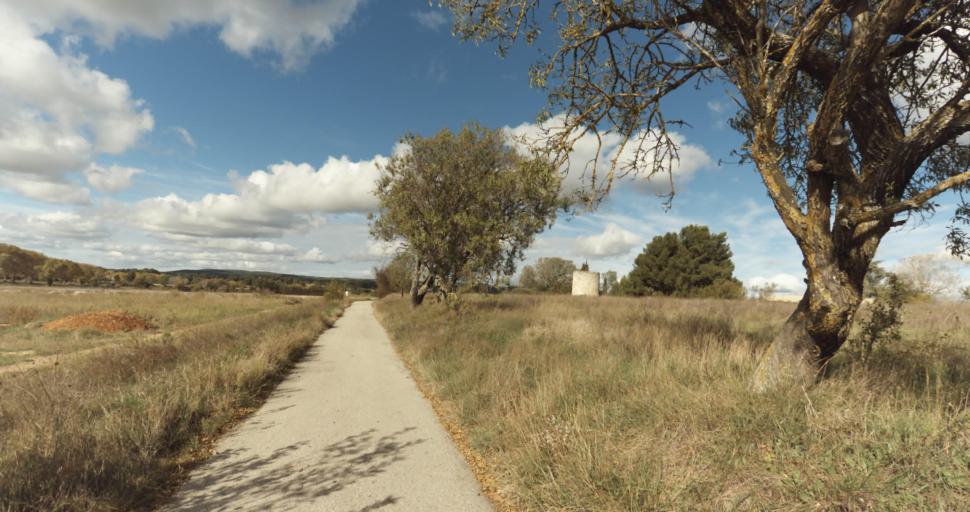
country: FR
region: Provence-Alpes-Cote d'Azur
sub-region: Departement des Bouches-du-Rhone
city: Venelles
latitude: 43.5825
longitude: 5.4849
